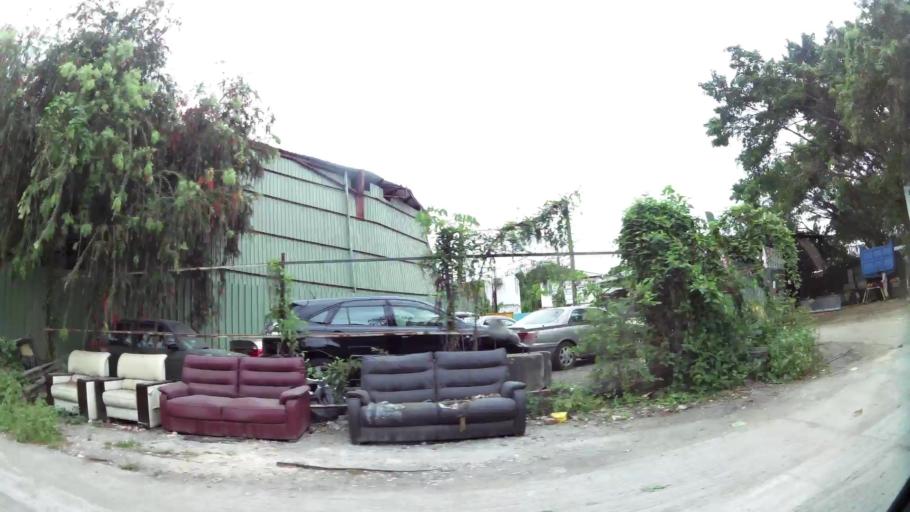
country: HK
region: Yuen Long
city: Yuen Long Kau Hui
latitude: 22.4437
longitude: 113.9913
